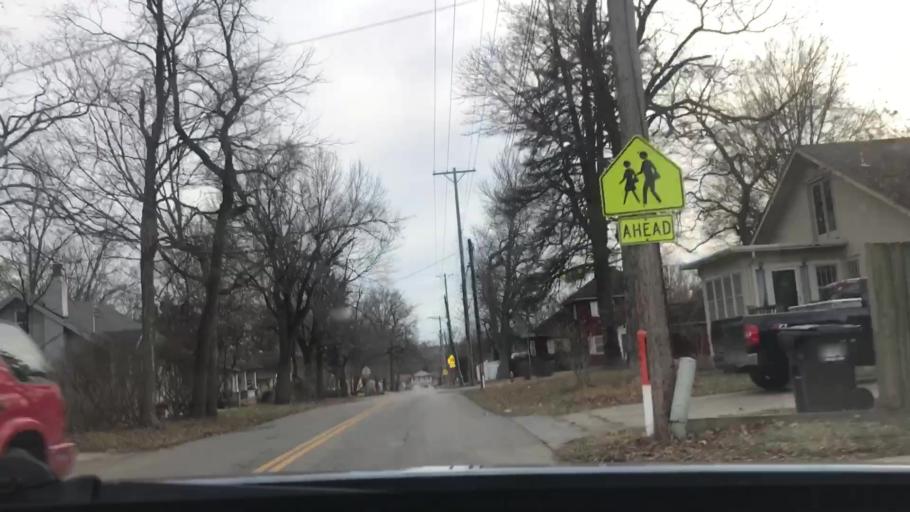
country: US
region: Missouri
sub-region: Jackson County
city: Independence
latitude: 39.0854
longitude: -94.4389
